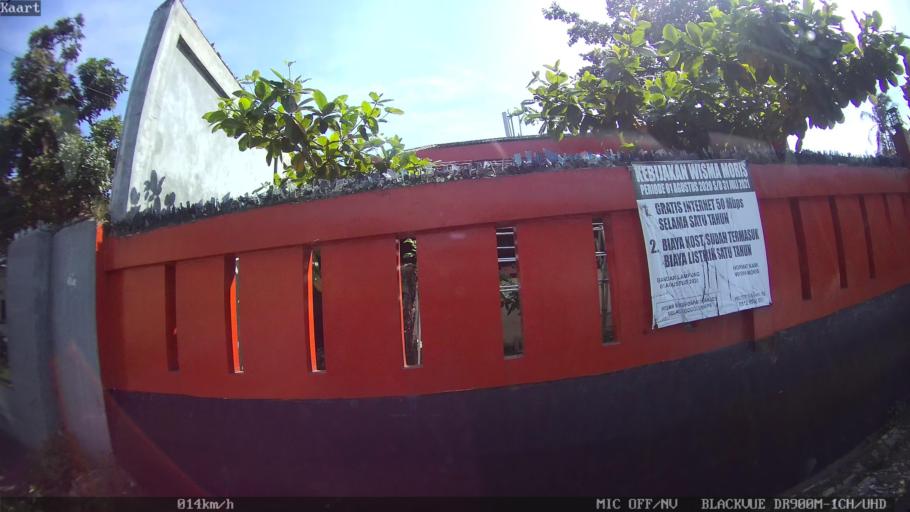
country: ID
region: Lampung
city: Kedaton
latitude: -5.3604
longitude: 105.2429
